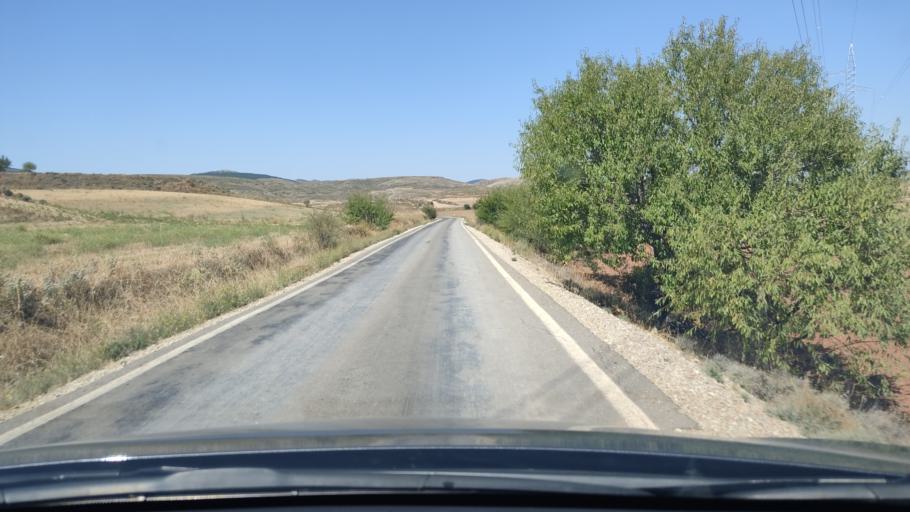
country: ES
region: Aragon
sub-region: Provincia de Teruel
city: Monforte de Moyuela
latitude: 41.0424
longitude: -0.9880
